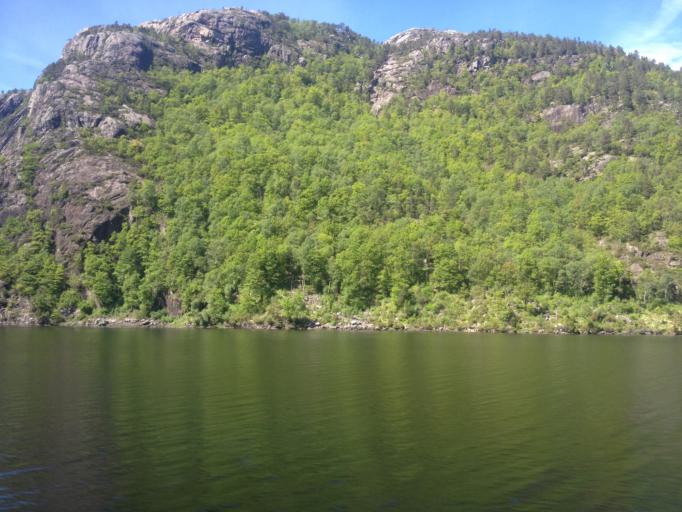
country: NO
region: Rogaland
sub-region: Lund
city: Moi
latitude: 58.4847
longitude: 6.4795
